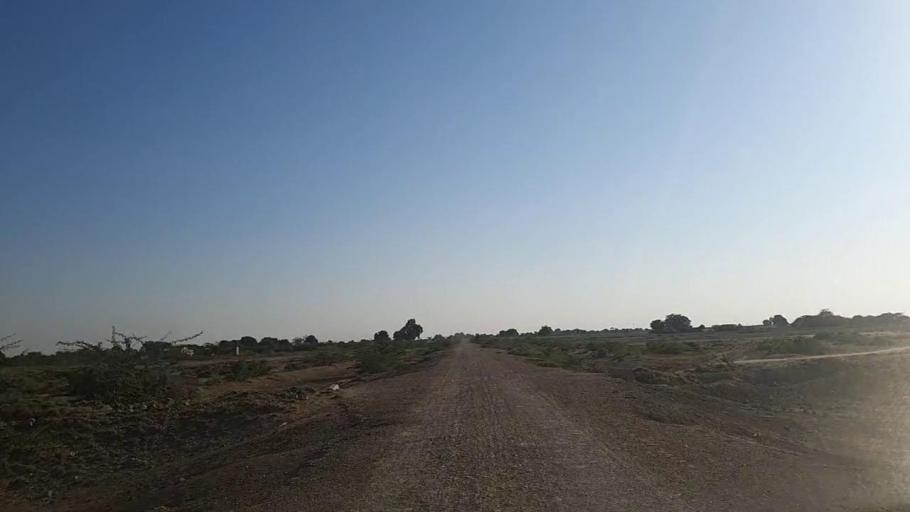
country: PK
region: Sindh
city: Naukot
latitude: 24.9537
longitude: 69.3879
